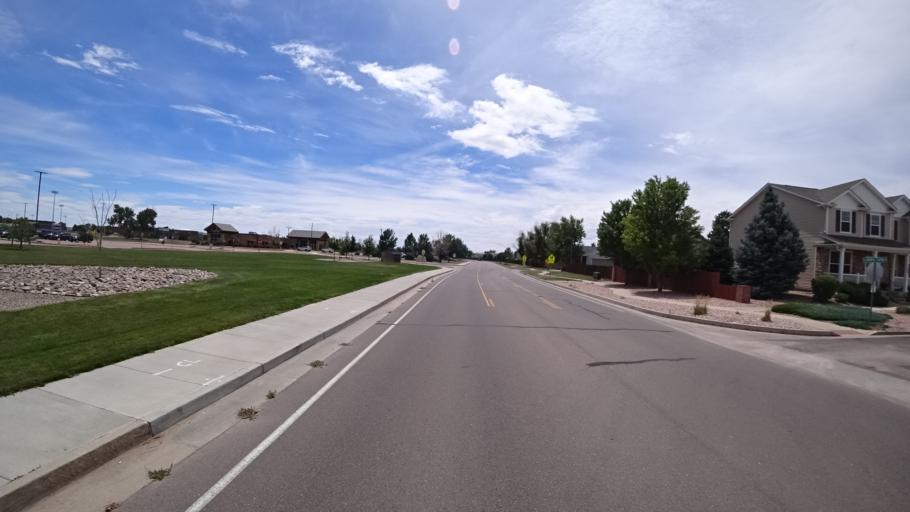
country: US
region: Colorado
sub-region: El Paso County
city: Fountain
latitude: 38.6769
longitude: -104.6874
